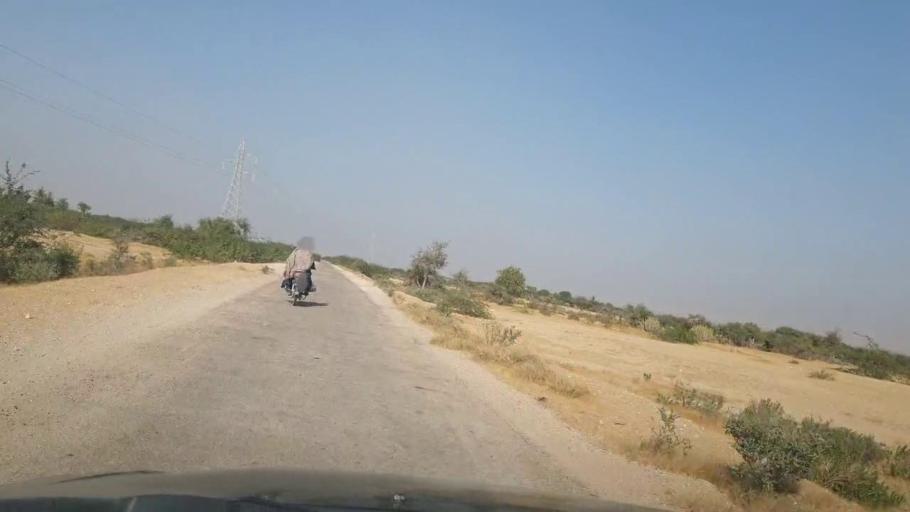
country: PK
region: Sindh
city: Jamshoro
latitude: 25.5334
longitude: 67.8238
